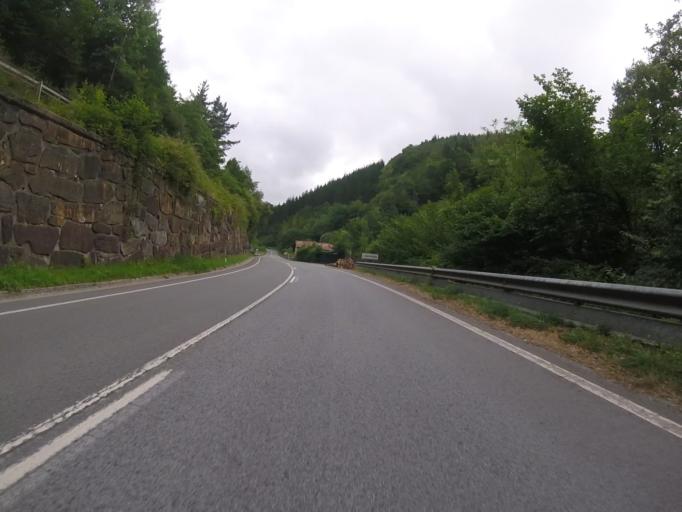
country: ES
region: Navarre
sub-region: Provincia de Navarra
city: Saldias
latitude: 43.1019
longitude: -1.7676
